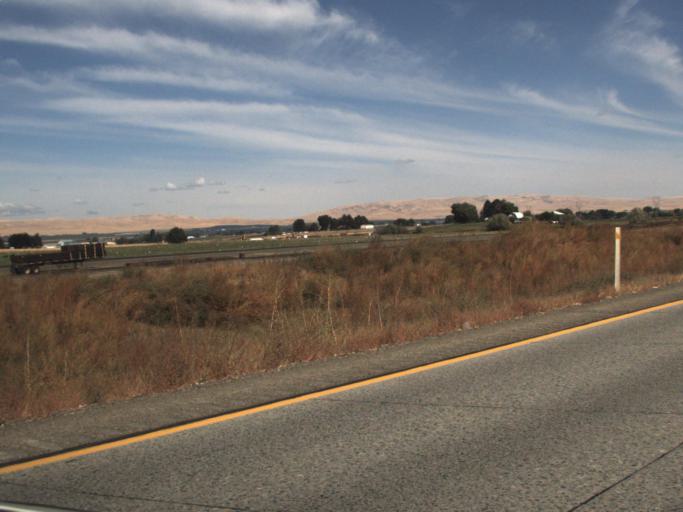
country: US
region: Washington
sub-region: Yakima County
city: Granger
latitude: 46.3382
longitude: -120.1466
